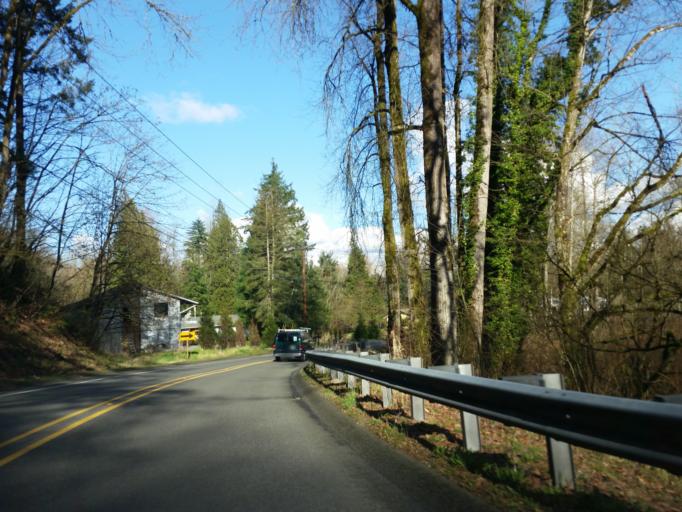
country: US
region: Washington
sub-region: Pierce County
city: McMillin
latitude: 47.1500
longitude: -122.2409
